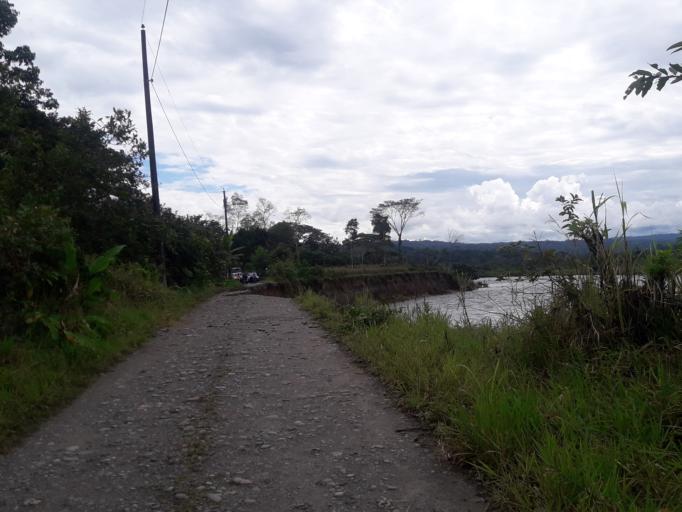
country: EC
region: Napo
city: Tena
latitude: -1.0641
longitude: -77.8166
